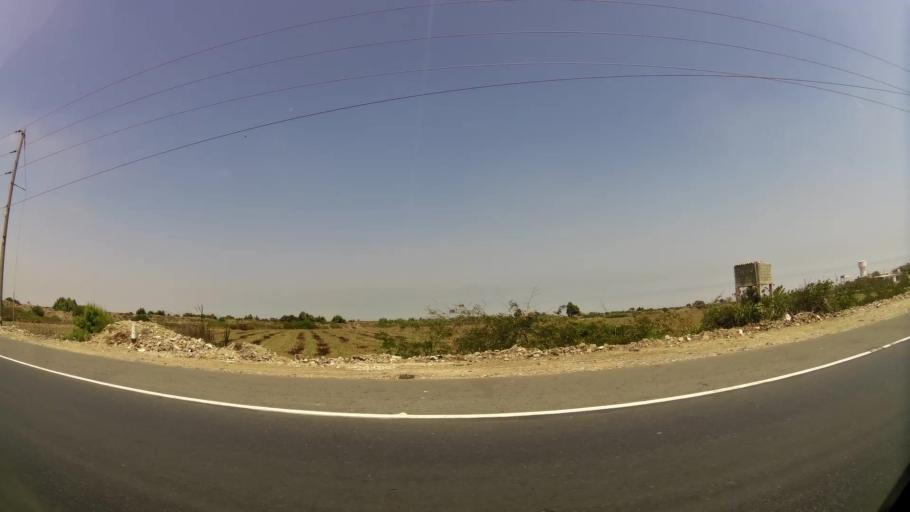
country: PE
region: La Libertad
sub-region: Provincia de Pacasmayo
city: Pacasmayo
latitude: -7.4195
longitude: -79.5440
